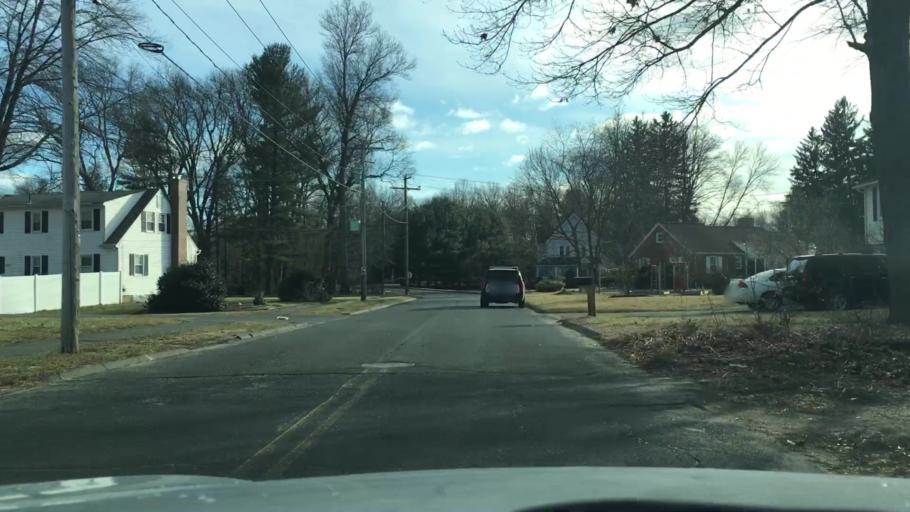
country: US
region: Massachusetts
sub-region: Hampden County
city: Agawam
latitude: 42.0642
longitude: -72.6281
